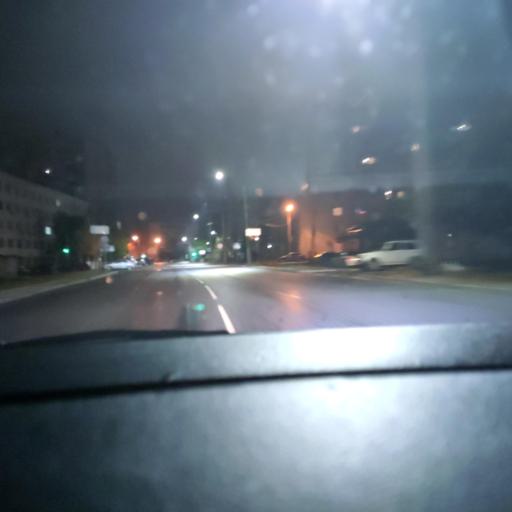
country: RU
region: Voronezj
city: Voronezh
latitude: 51.6514
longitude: 39.1866
